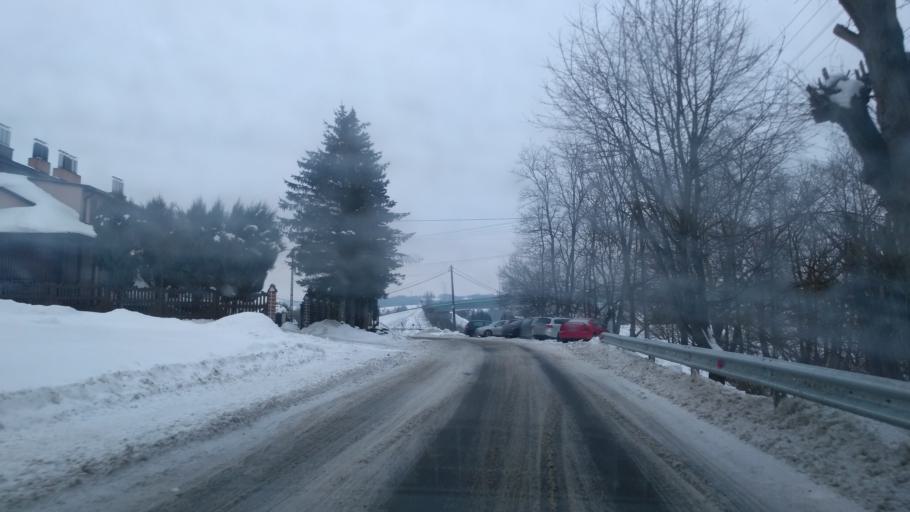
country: PL
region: Subcarpathian Voivodeship
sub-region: Powiat strzyzowski
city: Czudec
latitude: 49.9356
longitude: 21.8453
